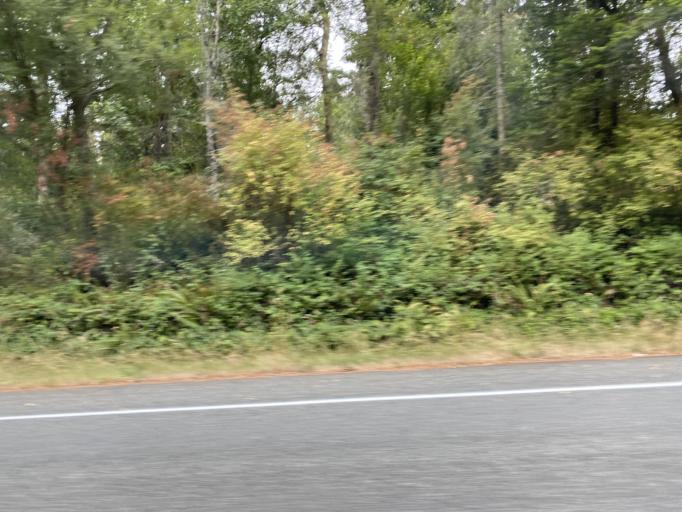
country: US
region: Washington
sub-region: Island County
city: Coupeville
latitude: 48.2192
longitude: -122.6414
